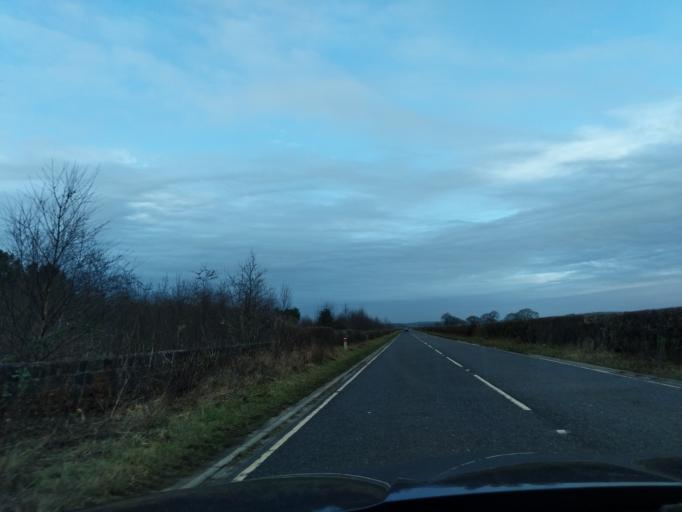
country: GB
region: England
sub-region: Northumberland
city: Meldon
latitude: 55.1069
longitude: -1.8488
